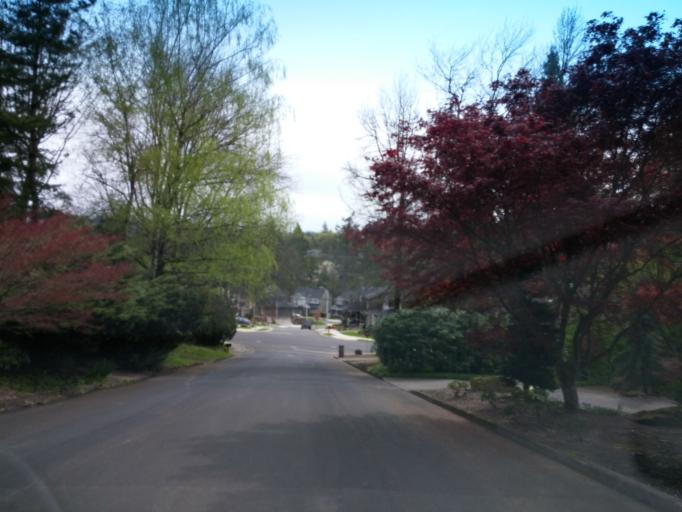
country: US
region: Oregon
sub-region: Washington County
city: Cedar Mill
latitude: 45.5360
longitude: -122.8005
